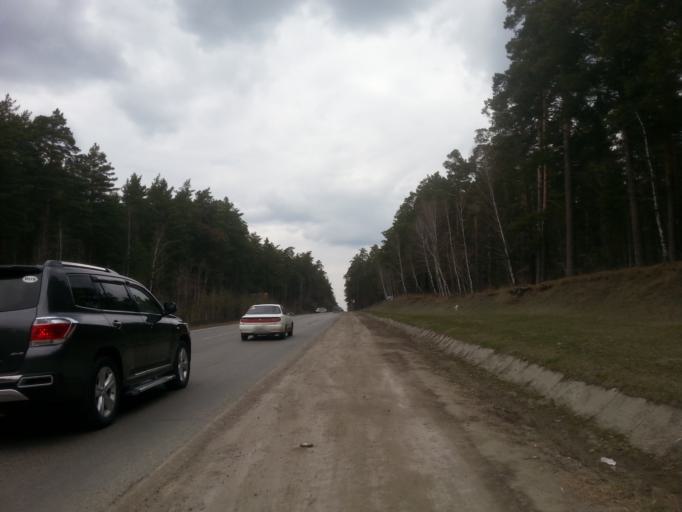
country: RU
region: Altai Krai
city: Yuzhnyy
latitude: 53.2698
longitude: 83.7253
